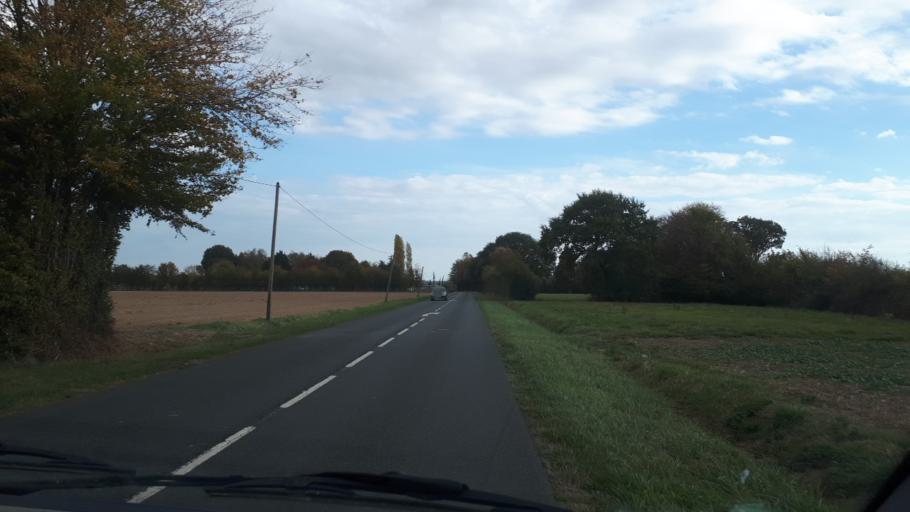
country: FR
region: Centre
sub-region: Departement du Loir-et-Cher
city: Mondoubleau
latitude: 48.0418
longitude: 0.9351
